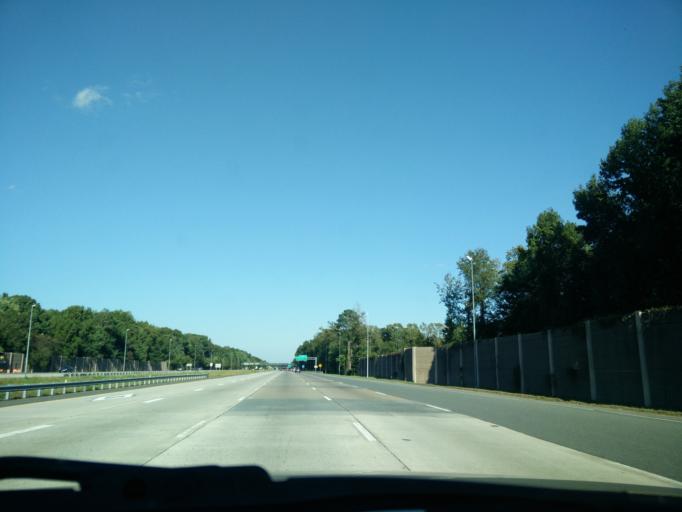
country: US
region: Virginia
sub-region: City of Chesapeake
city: Chesapeake
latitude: 36.7902
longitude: -76.2211
